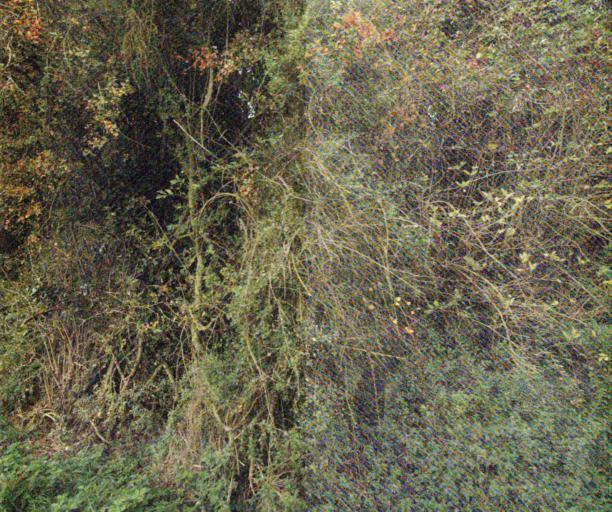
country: FR
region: Nord-Pas-de-Calais
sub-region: Departement du Nord
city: Aubers
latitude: 50.5818
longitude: 2.8128
